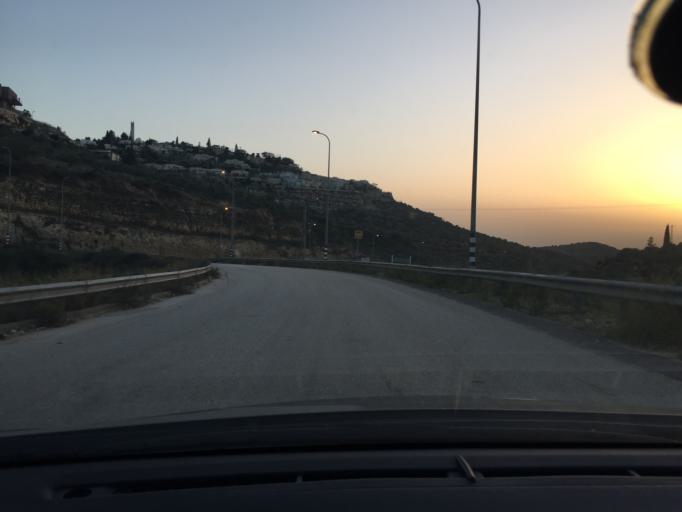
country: PS
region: West Bank
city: Rafat
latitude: 32.0666
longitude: 35.0525
